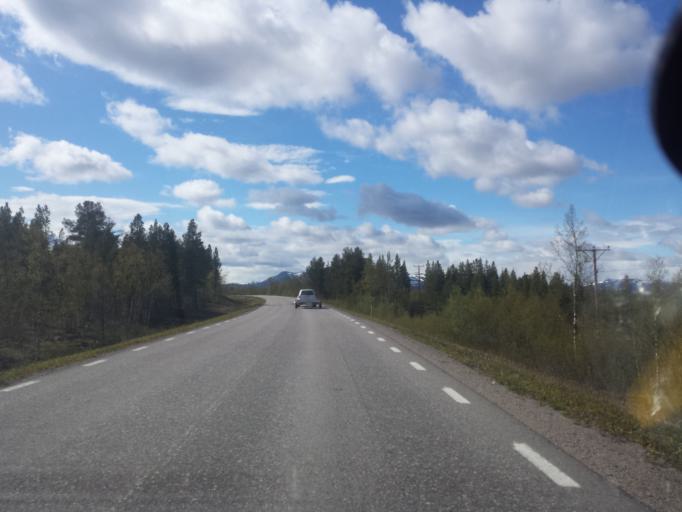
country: SE
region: Norrbotten
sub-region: Kiruna Kommun
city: Kiruna
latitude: 67.9939
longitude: 19.9074
